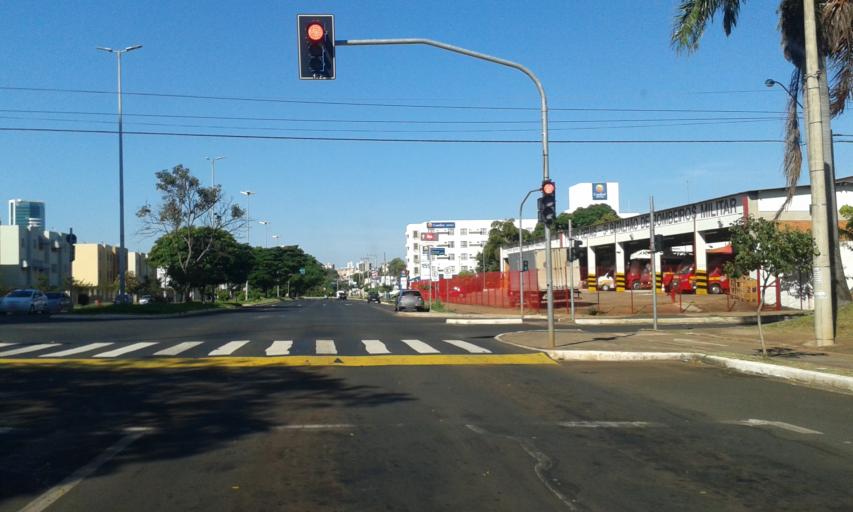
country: BR
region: Minas Gerais
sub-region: Uberlandia
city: Uberlandia
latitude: -18.8994
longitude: -48.2585
